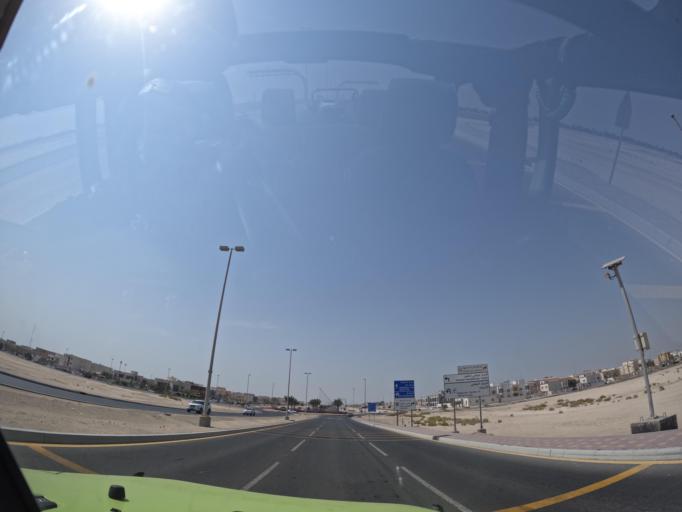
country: AE
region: Abu Dhabi
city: Abu Dhabi
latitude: 24.3427
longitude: 54.6332
